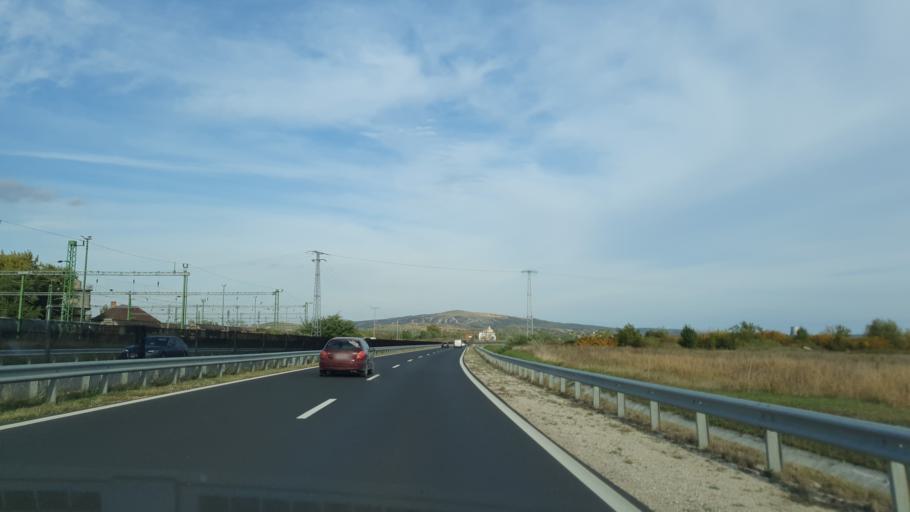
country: HU
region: Veszprem
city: Varpalota
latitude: 47.1932
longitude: 18.1448
